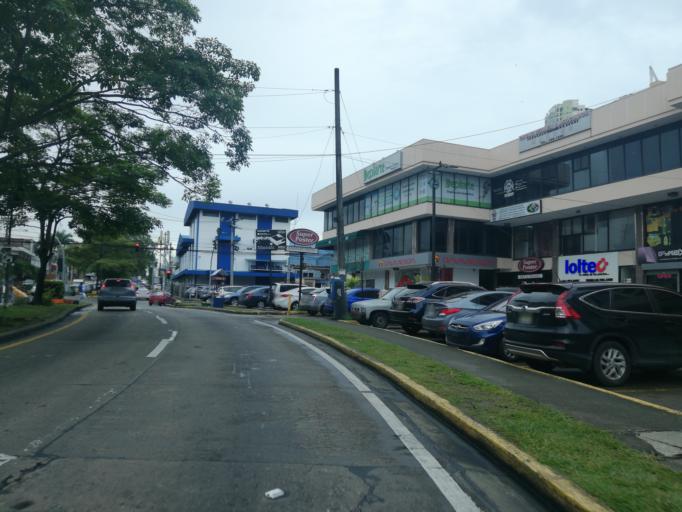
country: PA
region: Panama
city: Panama
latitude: 9.0066
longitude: -79.5367
